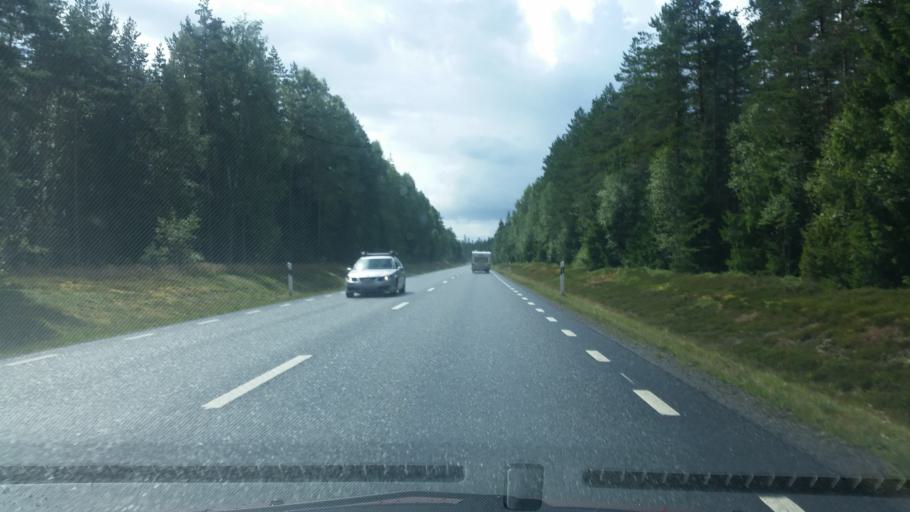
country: SE
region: Joenkoeping
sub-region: Gislaveds Kommun
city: Gislaved
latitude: 57.3864
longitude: 13.5856
